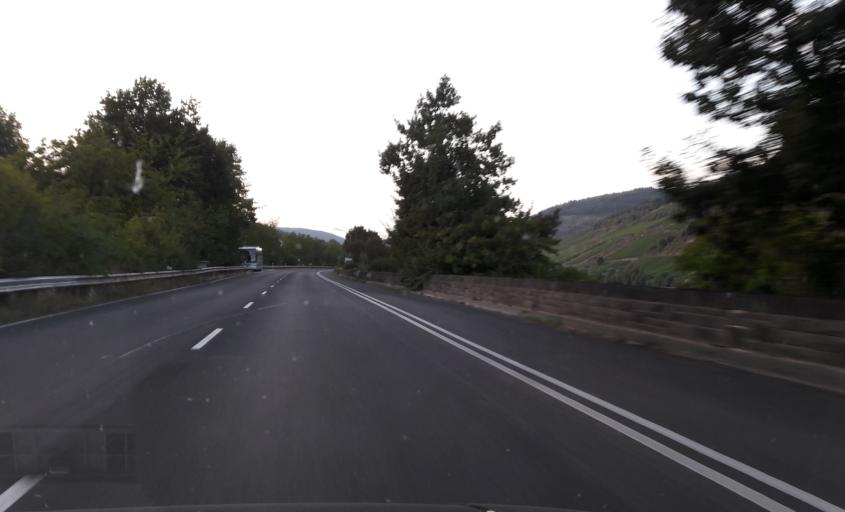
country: DE
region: Rheinland-Pfalz
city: Briedel
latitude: 50.0237
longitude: 7.1505
